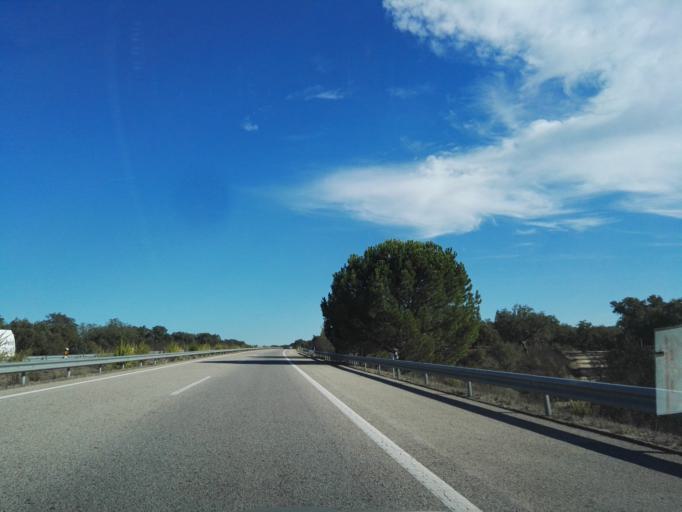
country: PT
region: Evora
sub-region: Vendas Novas
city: Vendas Novas
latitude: 38.6388
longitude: -8.3428
